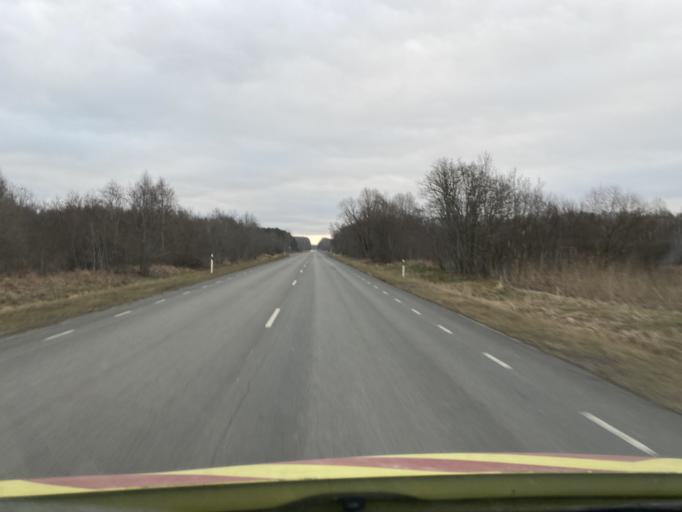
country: EE
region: Laeaene
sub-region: Lihula vald
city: Lihula
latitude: 58.8221
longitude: 23.7573
